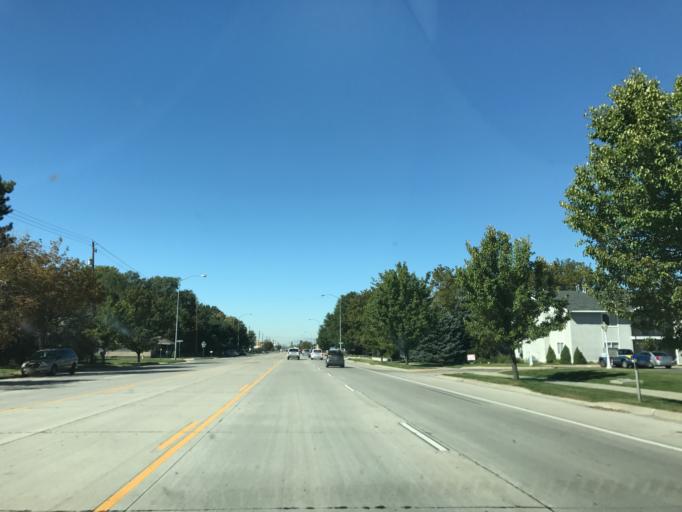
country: US
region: Utah
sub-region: Weber County
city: Ogden
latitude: 41.2443
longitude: -111.9630
